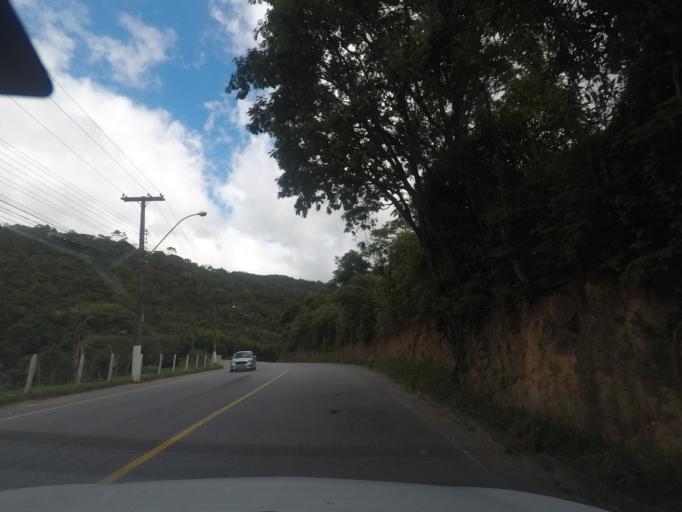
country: BR
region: Rio de Janeiro
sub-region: Teresopolis
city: Teresopolis
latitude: -22.3896
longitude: -42.9573
